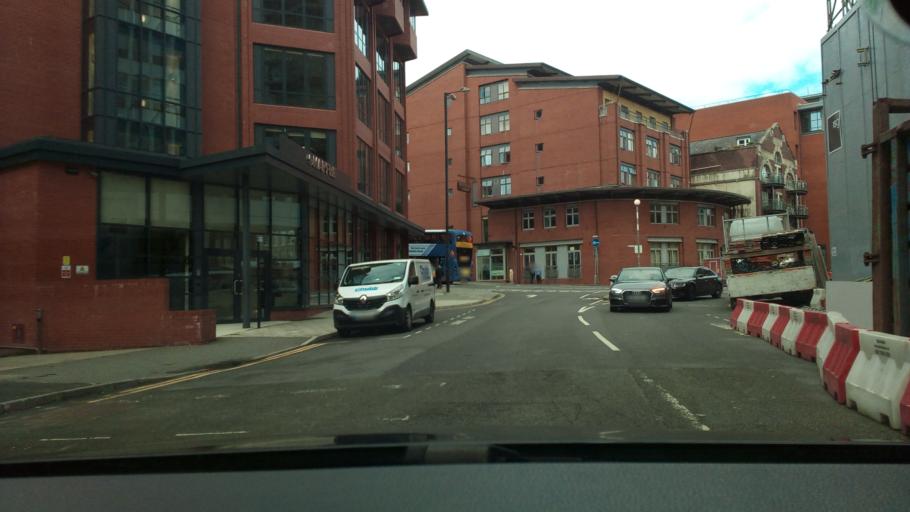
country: GB
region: England
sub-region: Bristol
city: Bristol
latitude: 51.4529
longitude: -2.5910
